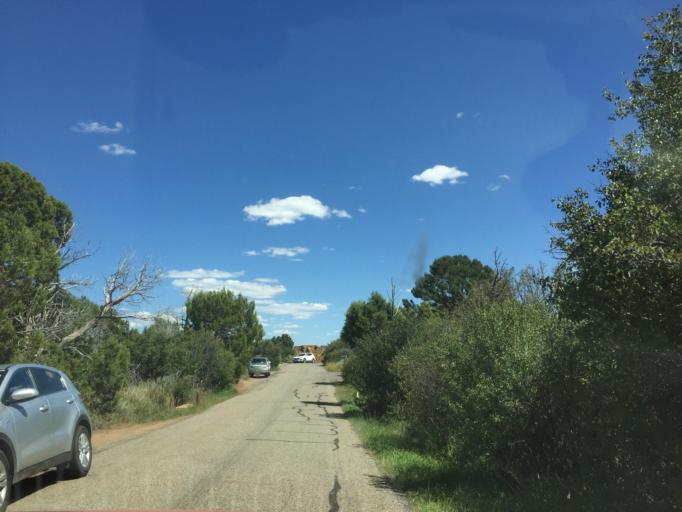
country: US
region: Colorado
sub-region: Montezuma County
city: Cortez
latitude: 37.2384
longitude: -108.5050
